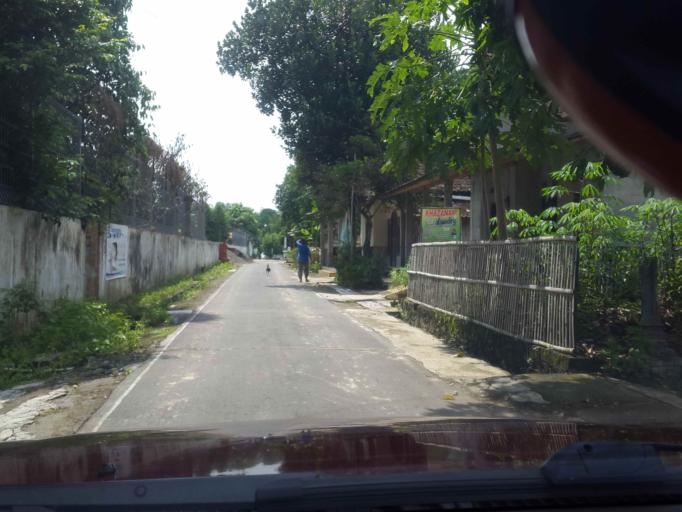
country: ID
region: Central Java
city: Jaten
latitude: -7.6021
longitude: 110.9438
